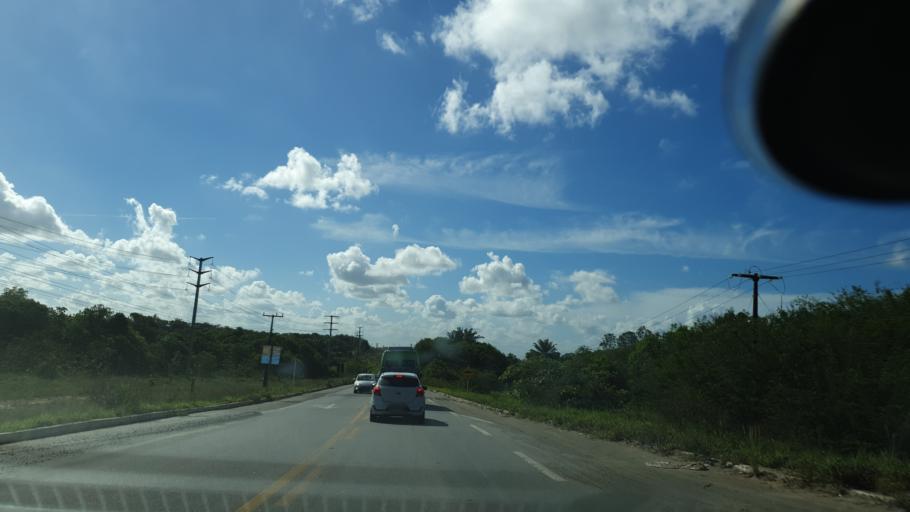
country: BR
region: Bahia
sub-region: Camacari
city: Camacari
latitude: -12.6838
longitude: -38.2327
